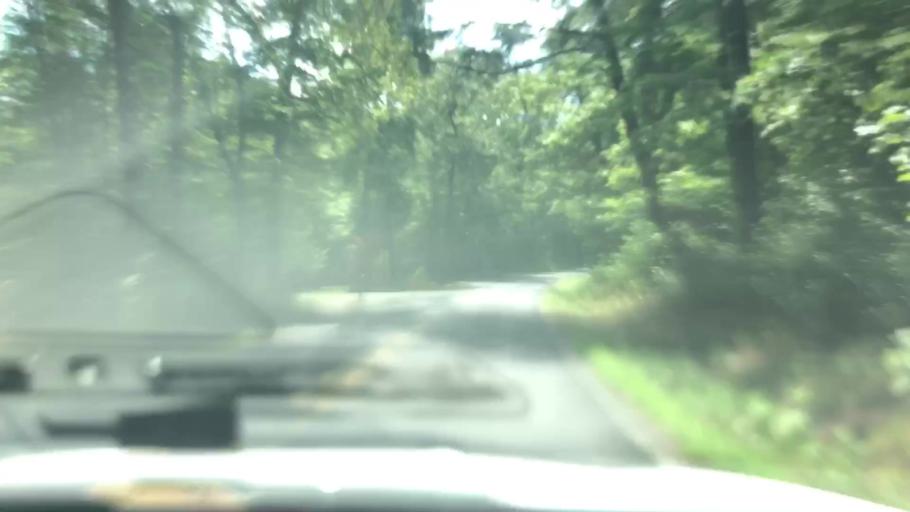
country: US
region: Virginia
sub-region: Middlesex County
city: Saluda
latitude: 37.6332
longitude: -76.6971
